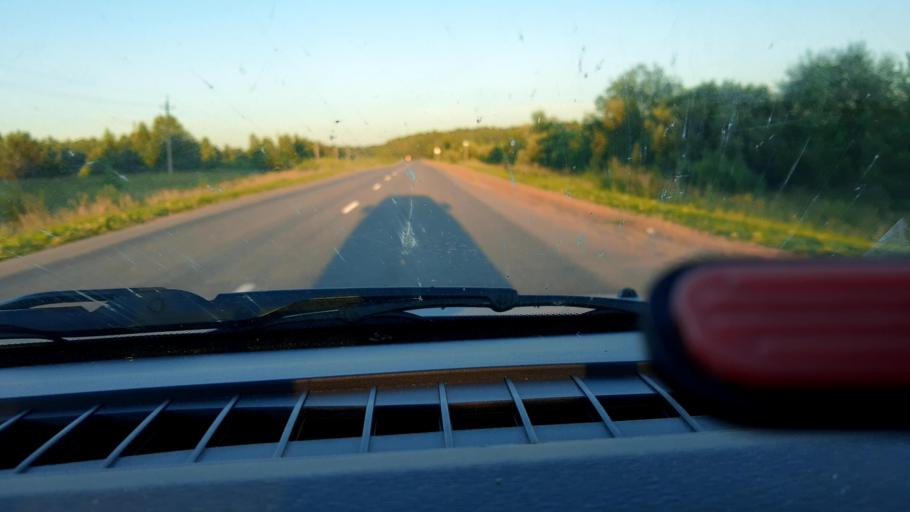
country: RU
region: Nizjnij Novgorod
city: Prudy
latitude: 57.3725
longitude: 46.1643
